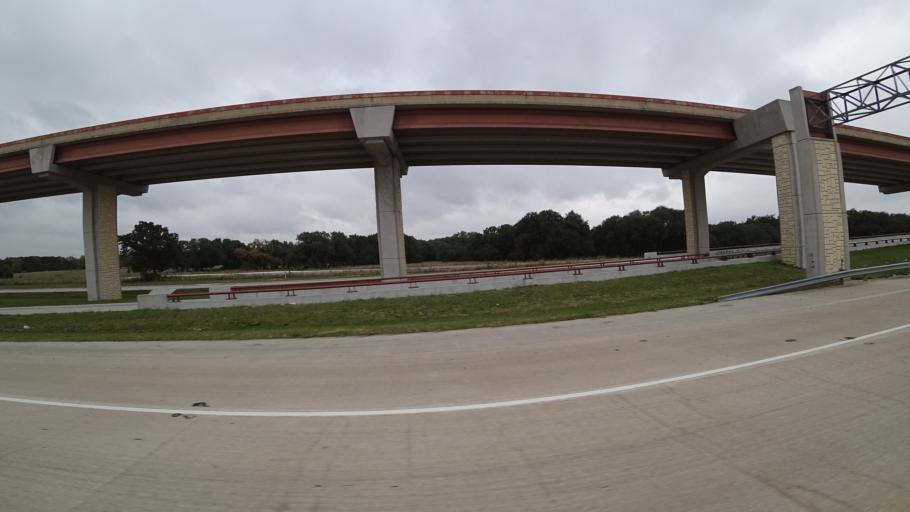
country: US
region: Texas
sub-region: Williamson County
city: Brushy Creek
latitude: 30.4794
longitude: -97.7123
